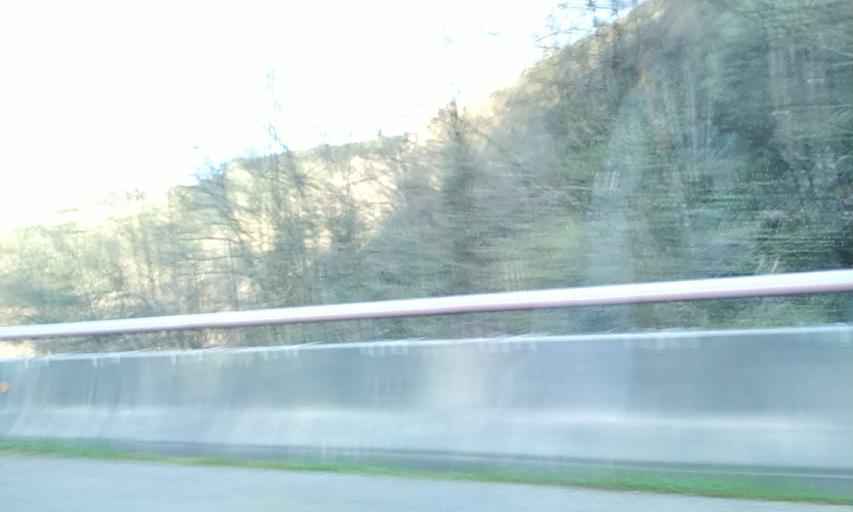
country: ES
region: Galicia
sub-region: Provincia de Lugo
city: Baralla
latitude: 42.9077
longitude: -7.2352
